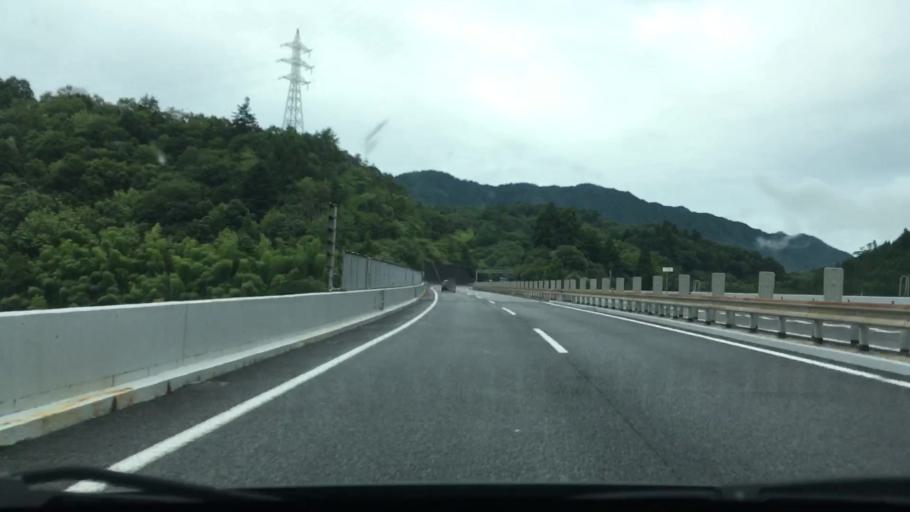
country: JP
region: Hiroshima
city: Hiroshima-shi
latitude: 34.5207
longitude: 132.4273
